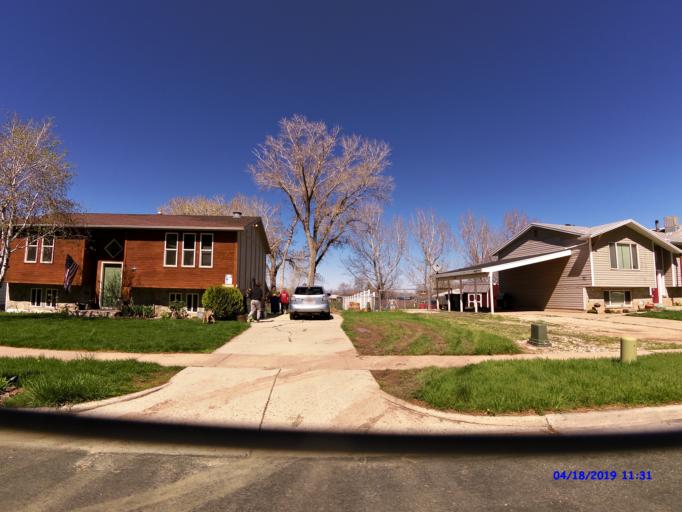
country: US
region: Utah
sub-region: Weber County
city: North Ogden
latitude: 41.2757
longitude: -111.9525
